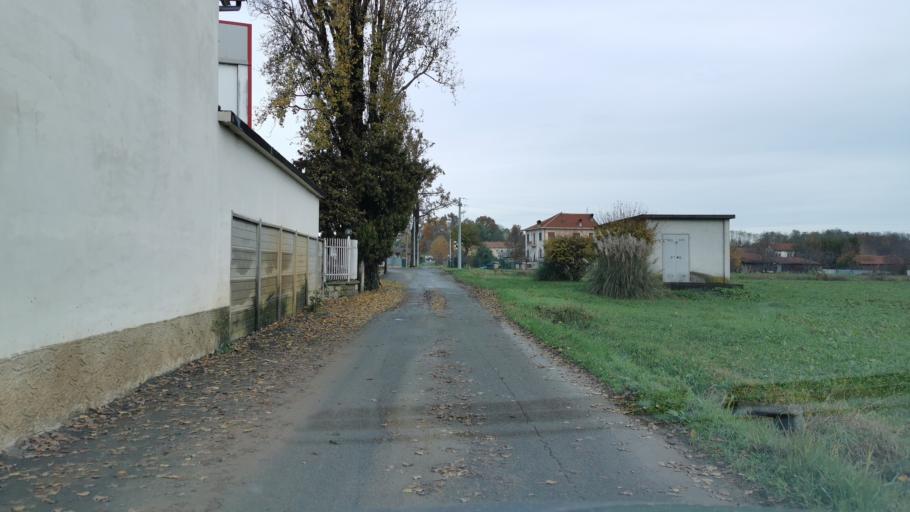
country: IT
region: Piedmont
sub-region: Provincia di Torino
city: San Francesco al Campo
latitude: 45.2135
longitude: 7.6777
